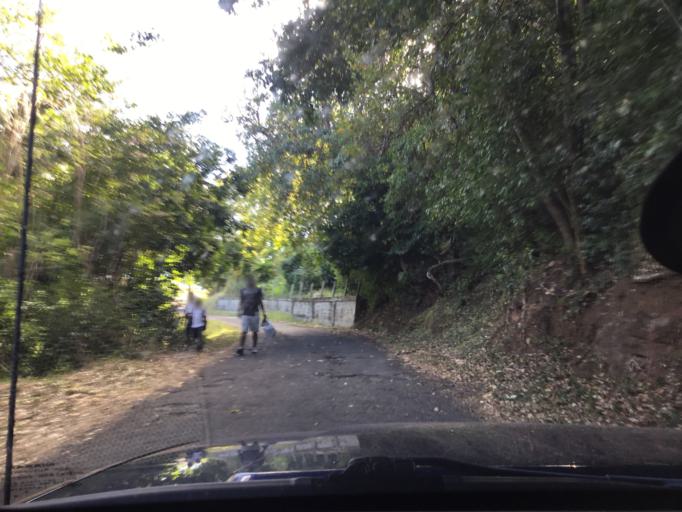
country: VC
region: Saint George
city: Kingstown
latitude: 13.1464
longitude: -61.1759
